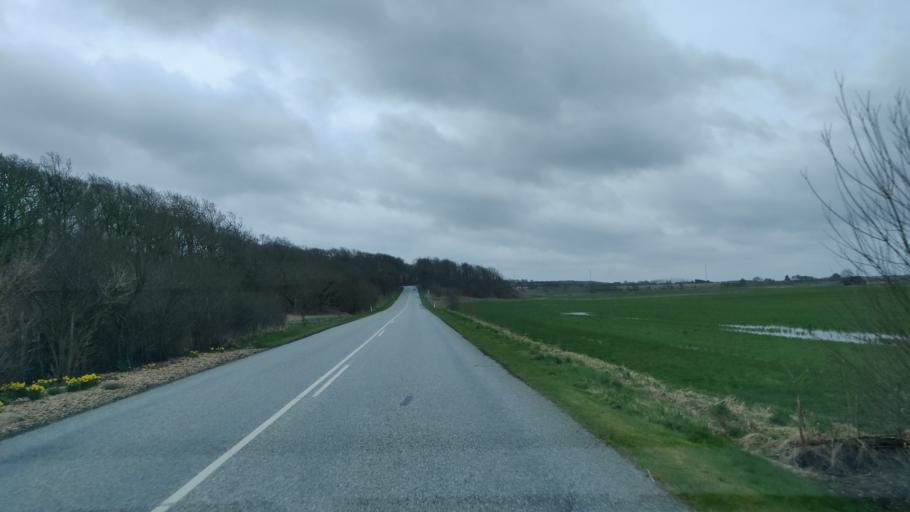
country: DK
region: Central Jutland
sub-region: Skive Kommune
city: Hojslev
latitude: 56.5610
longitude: 9.2482
